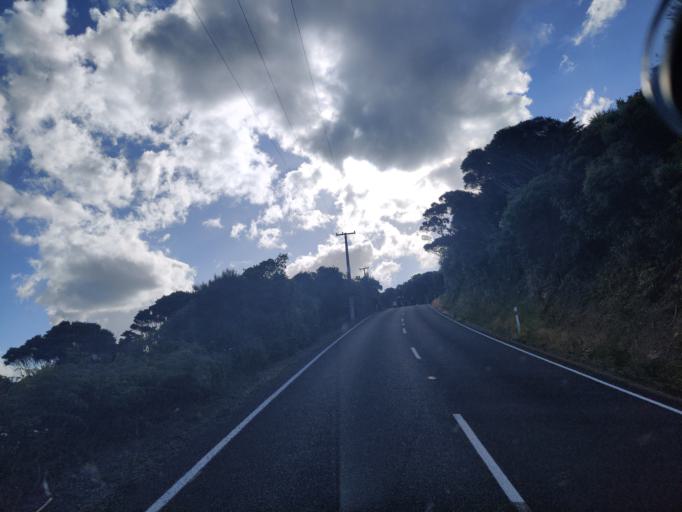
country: NZ
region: Northland
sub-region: Whangarei
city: Ngunguru
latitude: -35.6164
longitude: 174.5268
